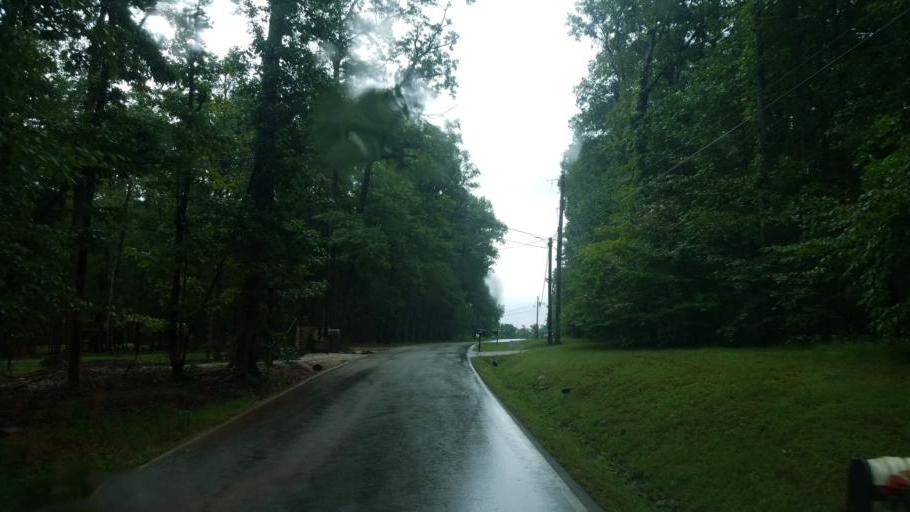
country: US
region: Kentucky
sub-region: Rowan County
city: Morehead
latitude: 38.1763
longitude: -83.4932
